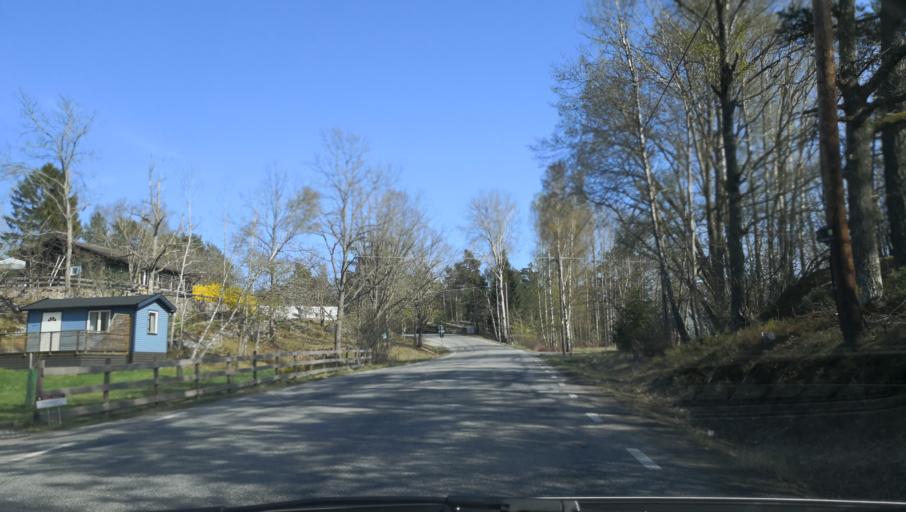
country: SE
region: Stockholm
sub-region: Varmdo Kommun
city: Holo
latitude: 59.3034
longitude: 18.6317
